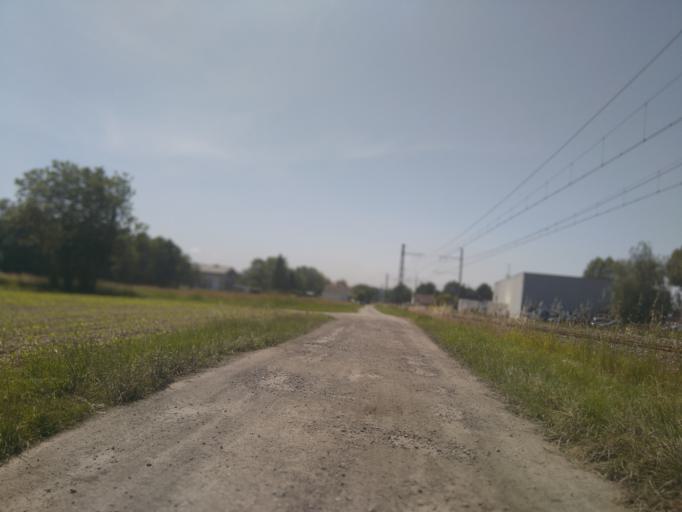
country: FR
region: Aquitaine
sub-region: Departement des Pyrenees-Atlantiques
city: Orthez
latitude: 43.4890
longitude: -0.7951
